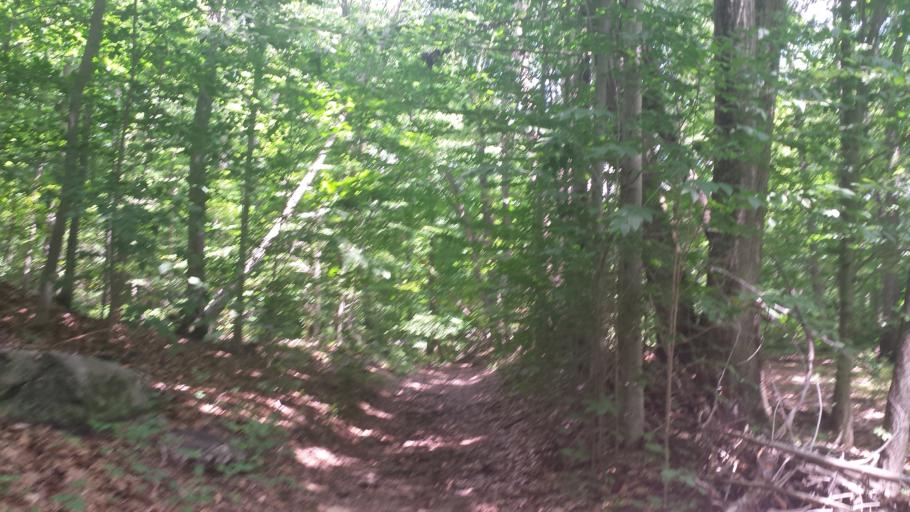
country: US
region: New York
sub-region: Westchester County
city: Scarsdale
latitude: 40.9889
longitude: -73.7503
